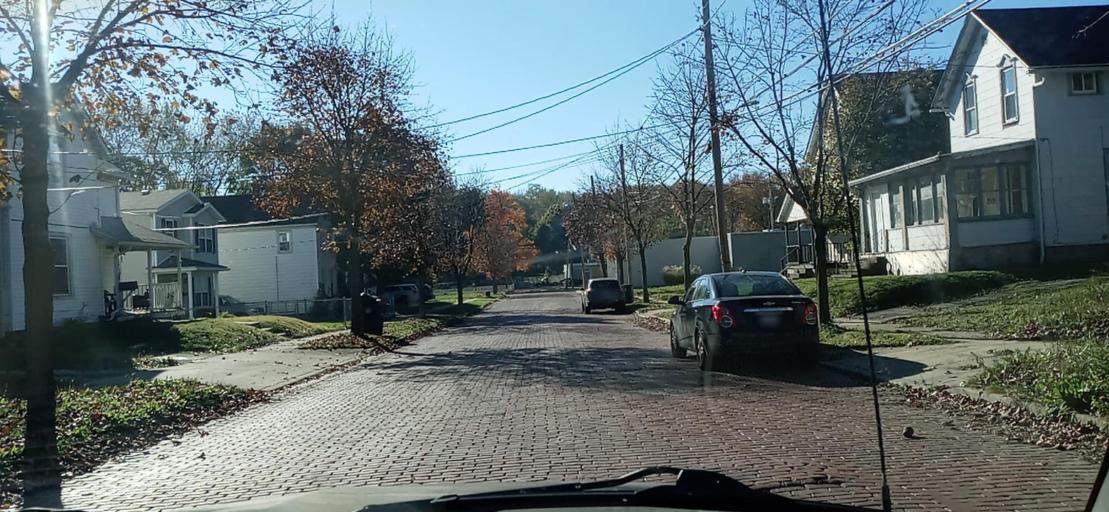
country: US
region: Ohio
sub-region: Summit County
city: Akron
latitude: 41.0685
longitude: -81.4952
